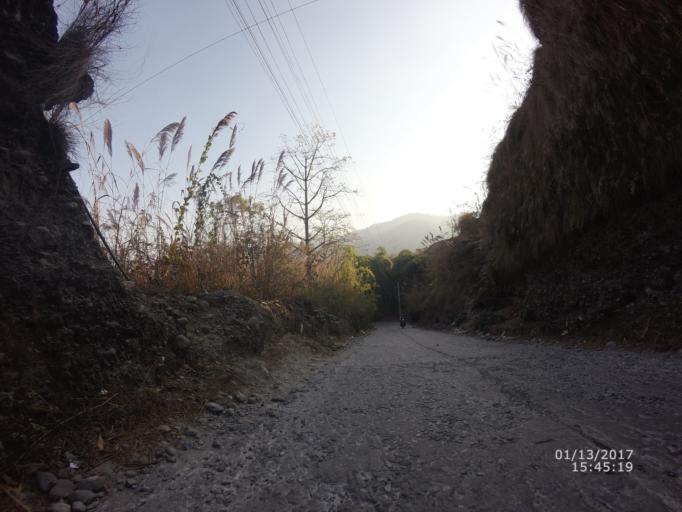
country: NP
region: Western Region
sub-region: Gandaki Zone
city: Pokhara
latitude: 28.1740
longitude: 83.9940
